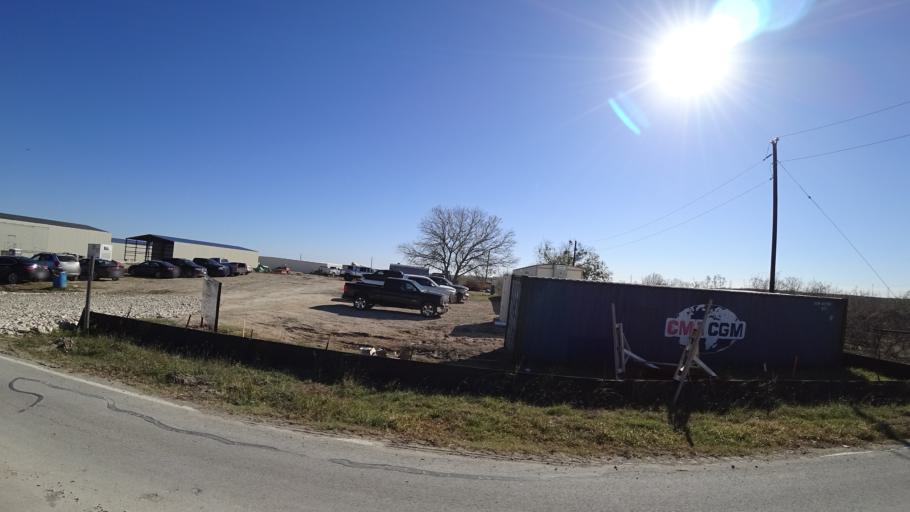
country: US
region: Texas
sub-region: Travis County
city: Onion Creek
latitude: 30.1182
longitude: -97.6700
